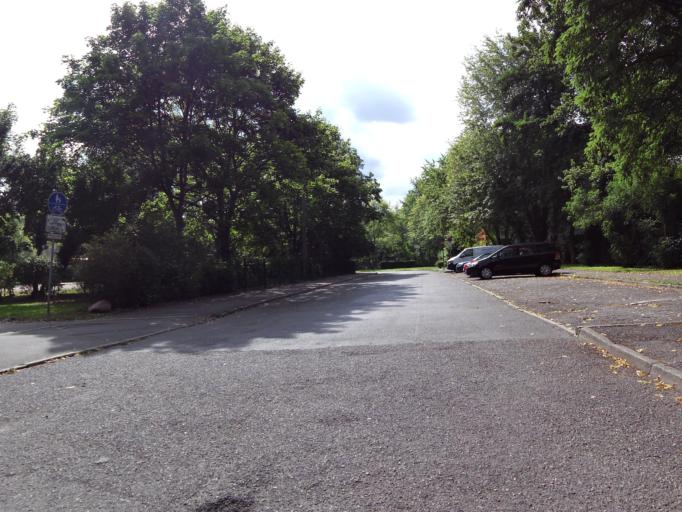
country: DE
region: Saxony
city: Leipzig
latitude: 51.3775
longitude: 12.4182
